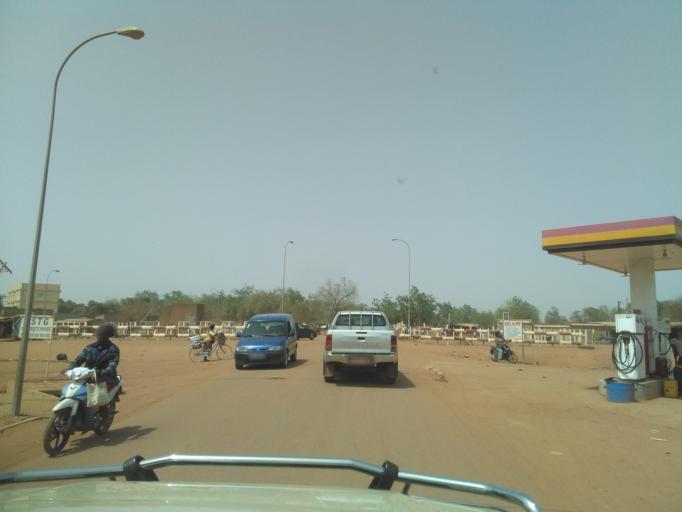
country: BF
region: Centre
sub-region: Kadiogo Province
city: Ouagadougou
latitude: 12.3964
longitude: -1.5526
